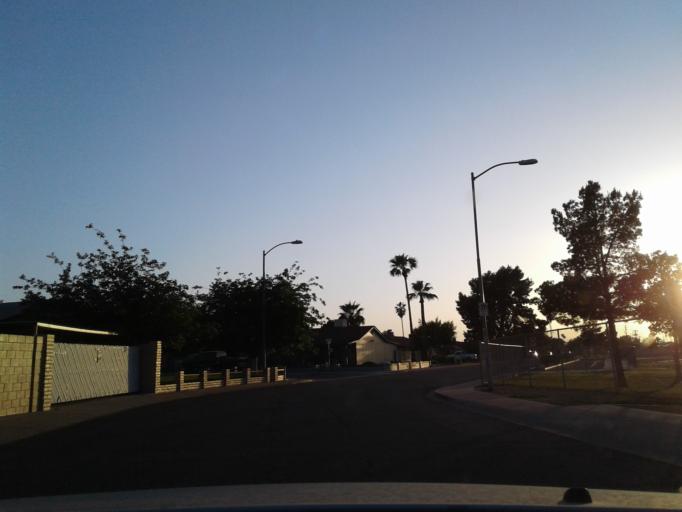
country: US
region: Arizona
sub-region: Maricopa County
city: Glendale
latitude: 33.6069
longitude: -112.0964
